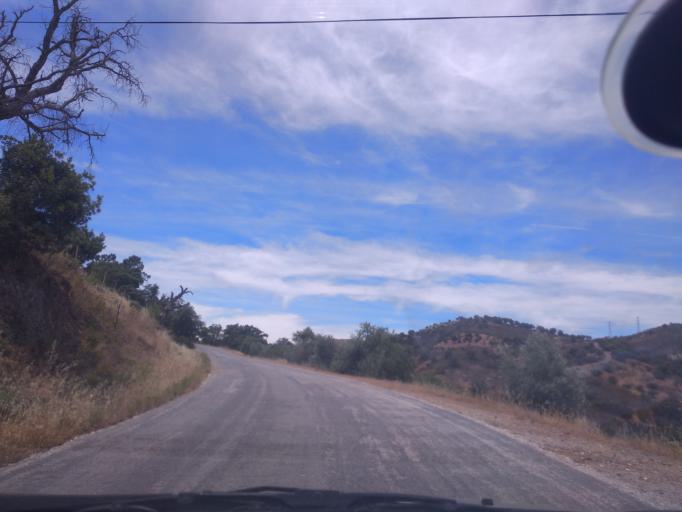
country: PT
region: Faro
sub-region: Sao Bras de Alportel
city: Sao Bras de Alportel
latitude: 37.1781
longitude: -7.8030
